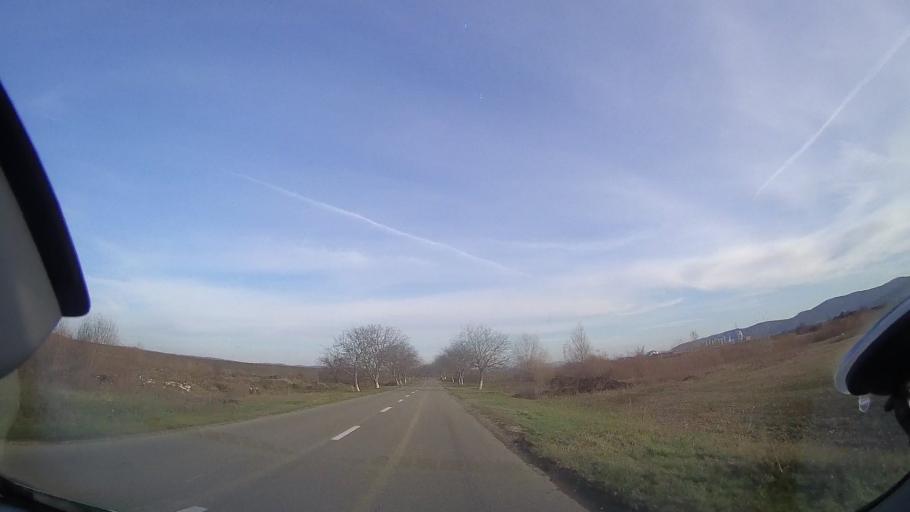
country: RO
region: Bihor
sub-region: Comuna Tetchea
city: Hotar
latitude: 47.0518
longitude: 22.2992
